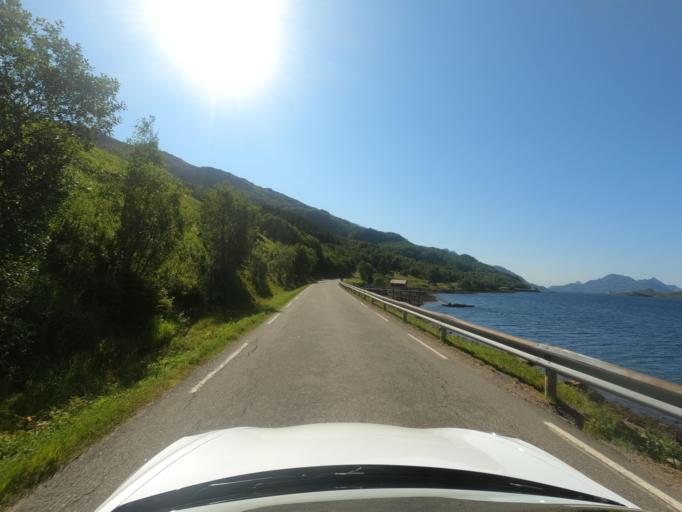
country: NO
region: Nordland
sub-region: Hadsel
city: Stokmarknes
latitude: 68.3836
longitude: 15.0896
